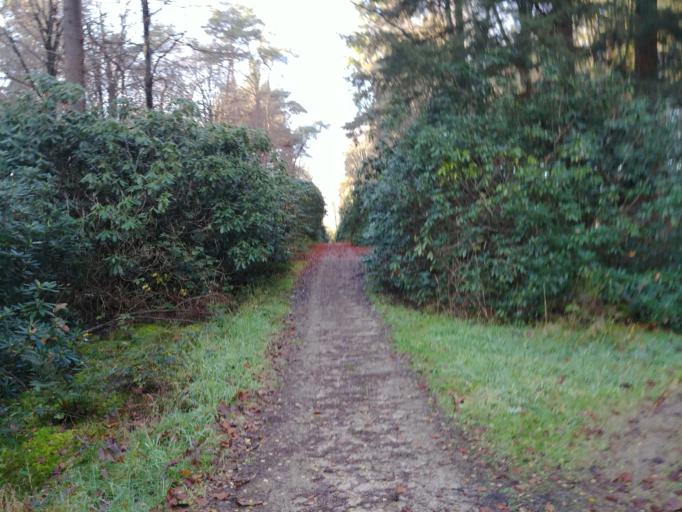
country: NL
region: Utrecht
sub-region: Gemeente Utrechtse Heuvelrug
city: Maarn
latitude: 52.0395
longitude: 5.3800
